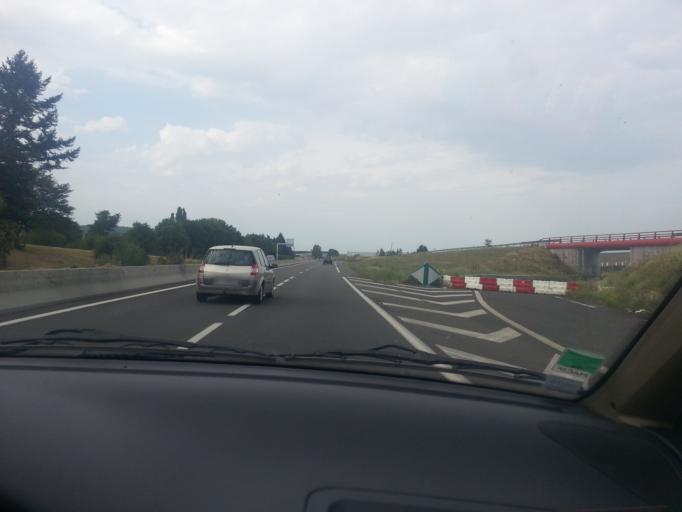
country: FR
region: Auvergne
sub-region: Departement du Puy-de-Dome
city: Cebazat
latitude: 45.8292
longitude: 3.1133
